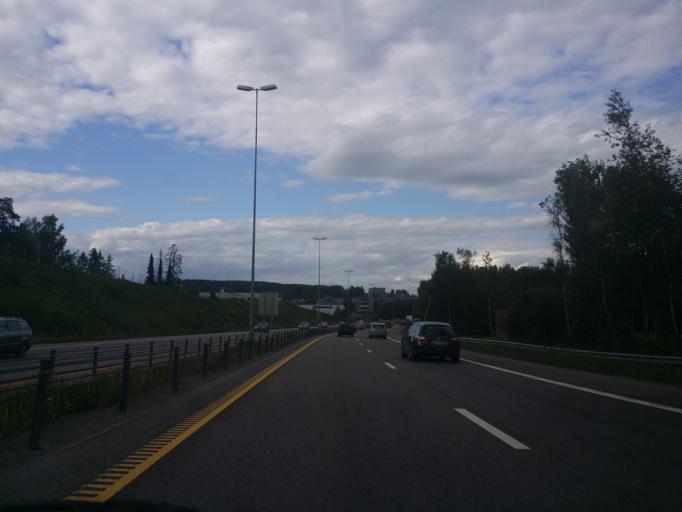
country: NO
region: Akershus
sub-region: Skedsmo
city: Leirsund
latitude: 60.0040
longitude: 11.0467
